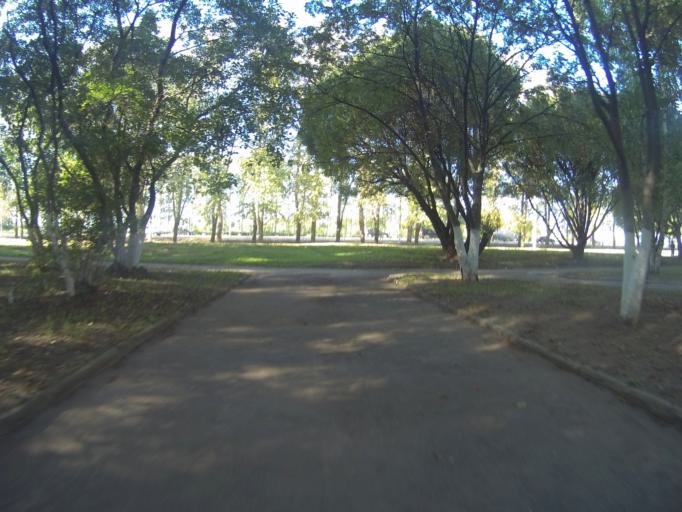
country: RU
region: Vladimir
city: Kommunar
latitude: 56.1730
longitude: 40.4566
